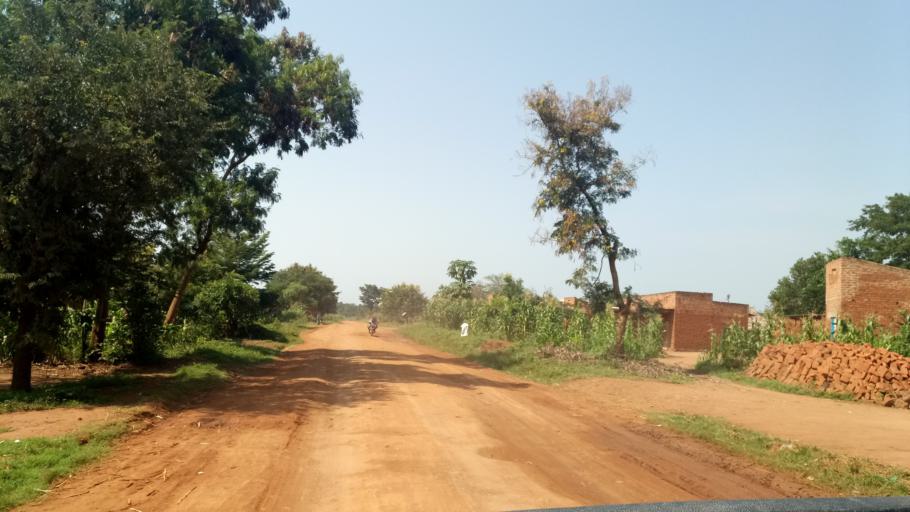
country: UG
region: Eastern Region
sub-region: Kaliro District
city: Kaliro
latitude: 0.9586
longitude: 33.4717
